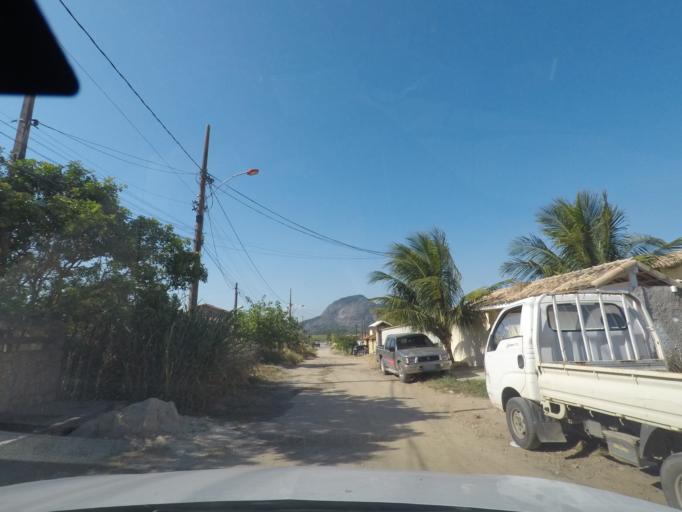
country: BR
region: Rio de Janeiro
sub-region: Marica
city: Marica
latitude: -22.9684
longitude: -42.9164
